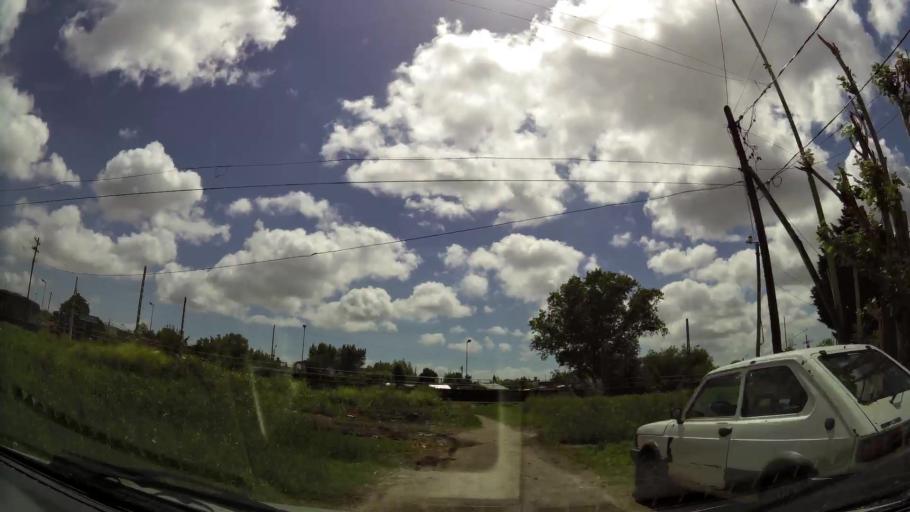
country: AR
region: Buenos Aires
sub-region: Partido de Quilmes
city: Quilmes
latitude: -34.8257
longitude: -58.2124
